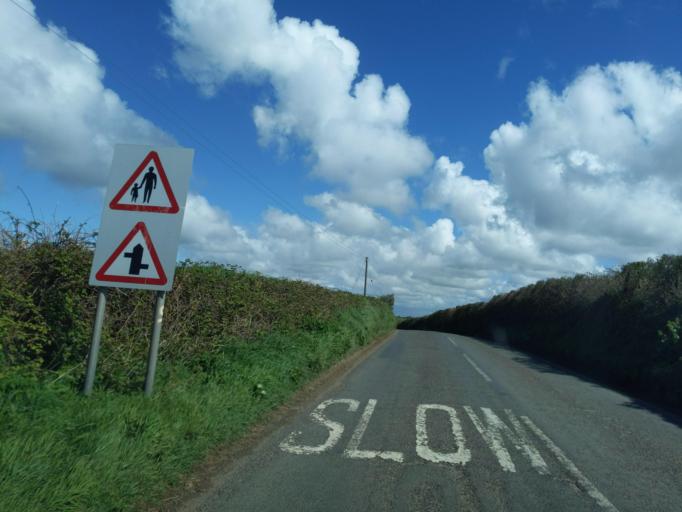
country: GB
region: England
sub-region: Cornwall
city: Wadebridge
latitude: 50.5733
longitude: -4.8335
